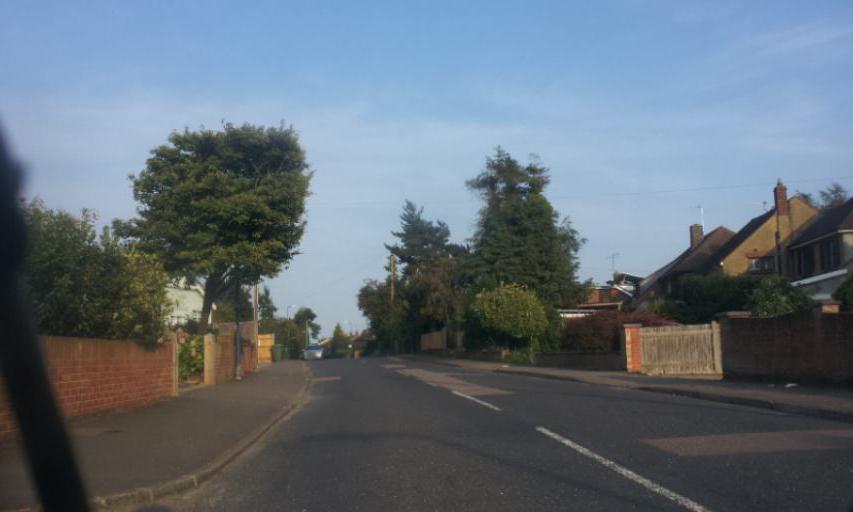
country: GB
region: England
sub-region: Kent
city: Aylesford
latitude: 51.2678
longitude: 0.4767
